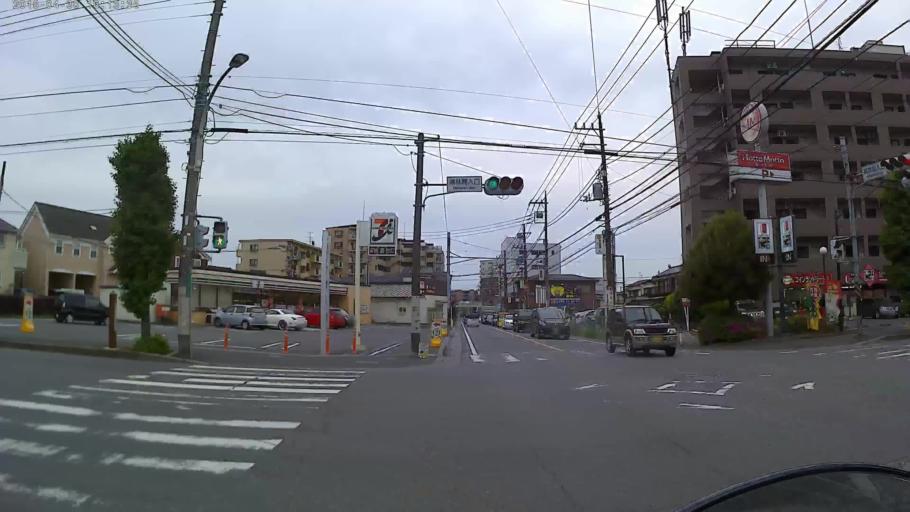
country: JP
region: Kanagawa
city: Minami-rinkan
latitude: 35.4902
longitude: 139.4313
